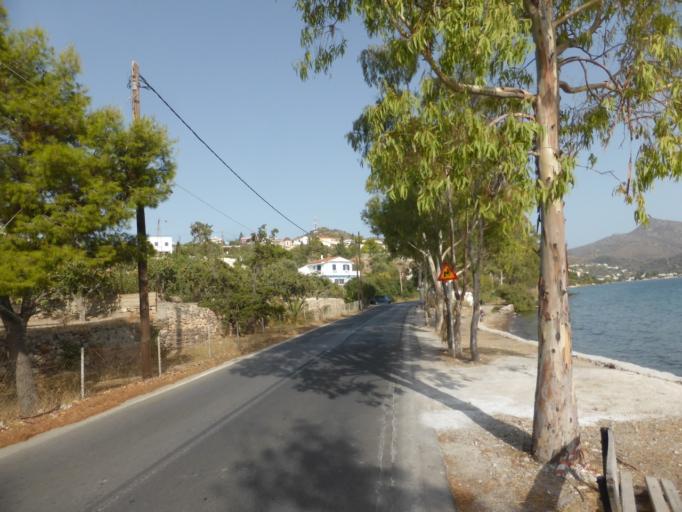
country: GR
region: Attica
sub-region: Nomos Piraios
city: Aegina
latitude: 37.7250
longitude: 23.4471
